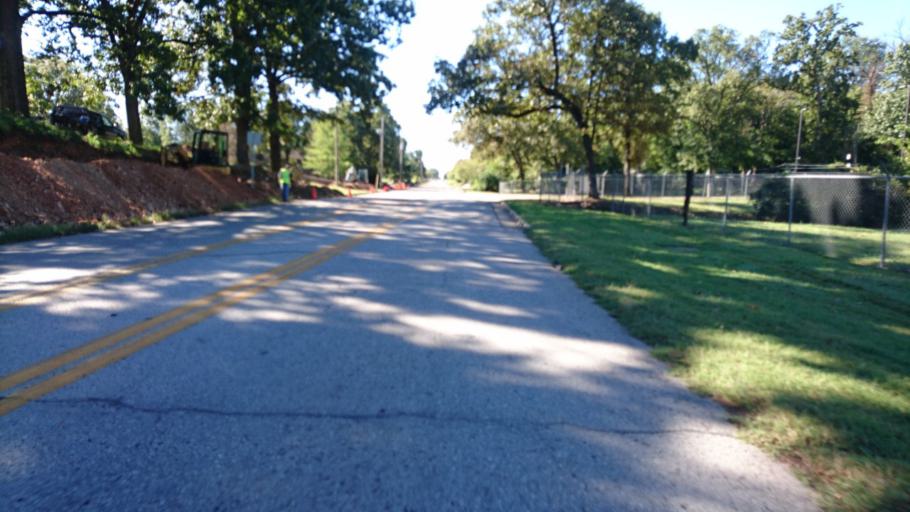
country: US
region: Missouri
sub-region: Jasper County
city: Joplin
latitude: 37.0956
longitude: -94.4946
